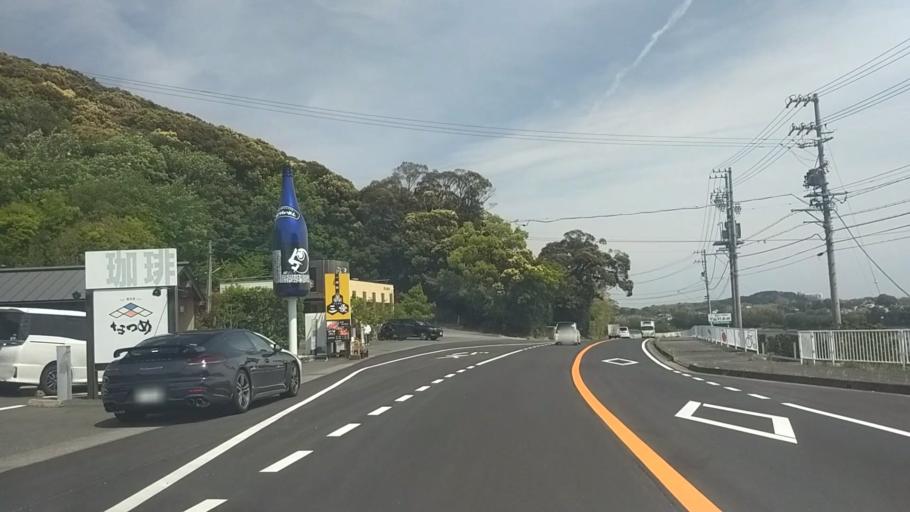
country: JP
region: Shizuoka
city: Kosai-shi
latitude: 34.7971
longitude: 137.5634
